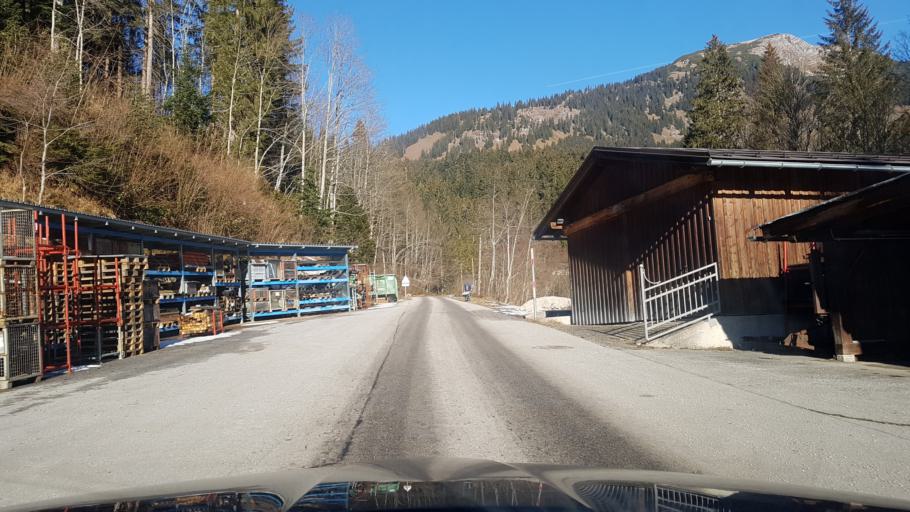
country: AT
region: Salzburg
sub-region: Politischer Bezirk Salzburg-Umgebung
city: Strobl
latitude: 47.5961
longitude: 13.4648
